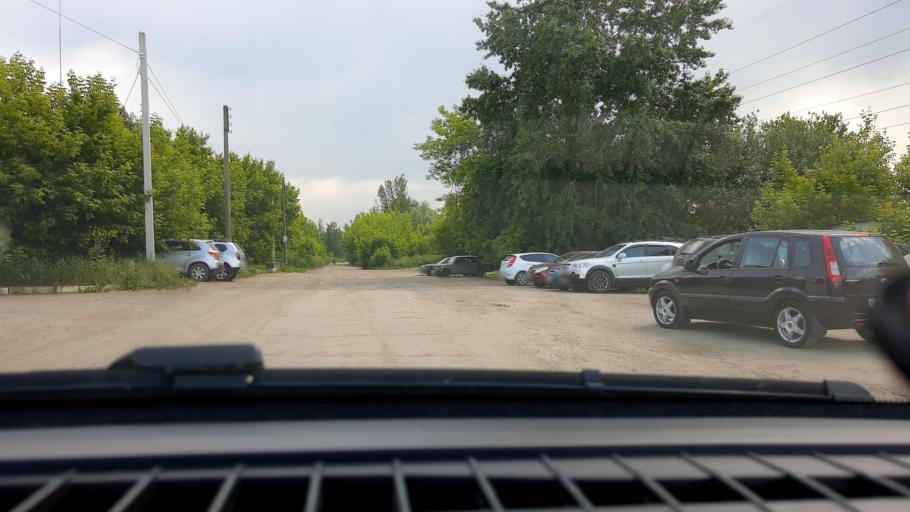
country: RU
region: Nizjnij Novgorod
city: Gorbatovka
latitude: 56.2700
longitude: 43.8487
